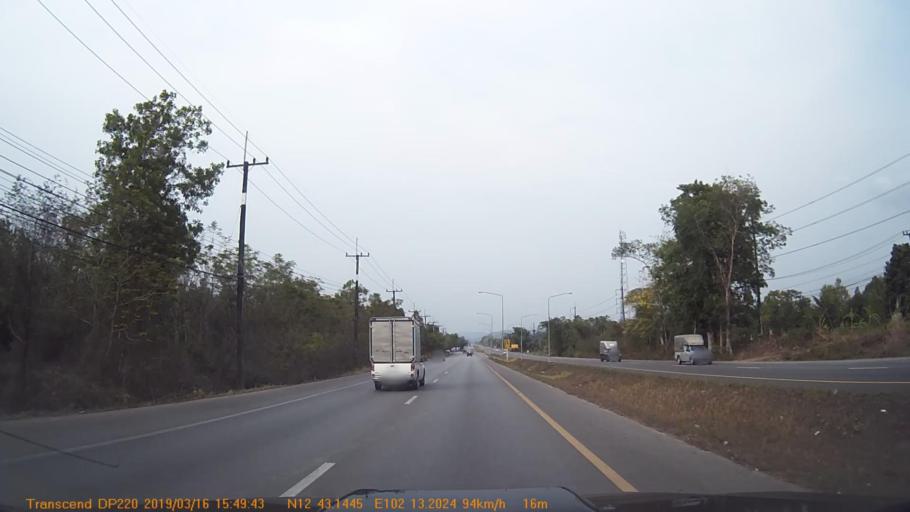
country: TH
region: Chanthaburi
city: Makham
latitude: 12.7193
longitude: 102.2202
